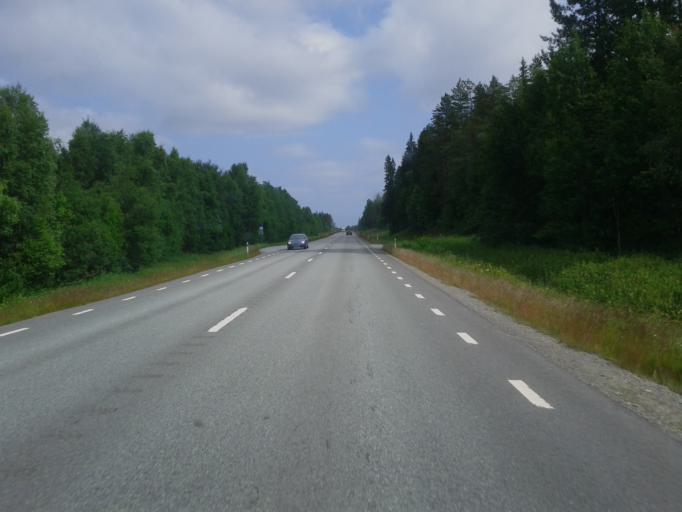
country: SE
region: Vaesterbotten
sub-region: Skelleftea Kommun
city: Burea
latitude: 64.3394
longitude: 21.2763
